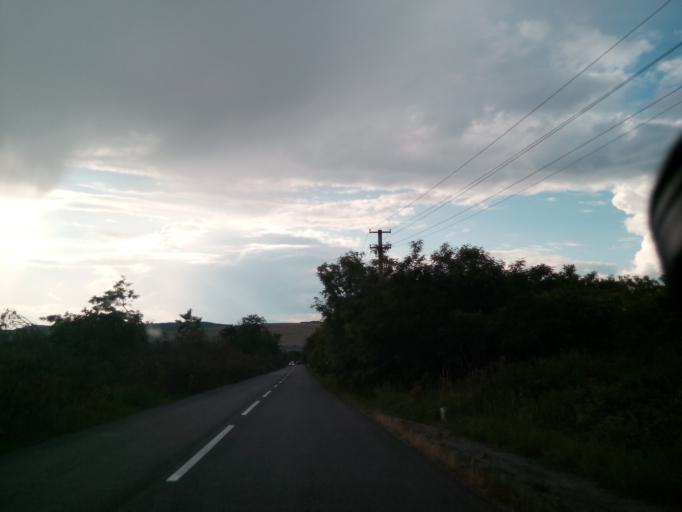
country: SK
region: Kosicky
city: Kosice
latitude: 48.6489
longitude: 21.4101
